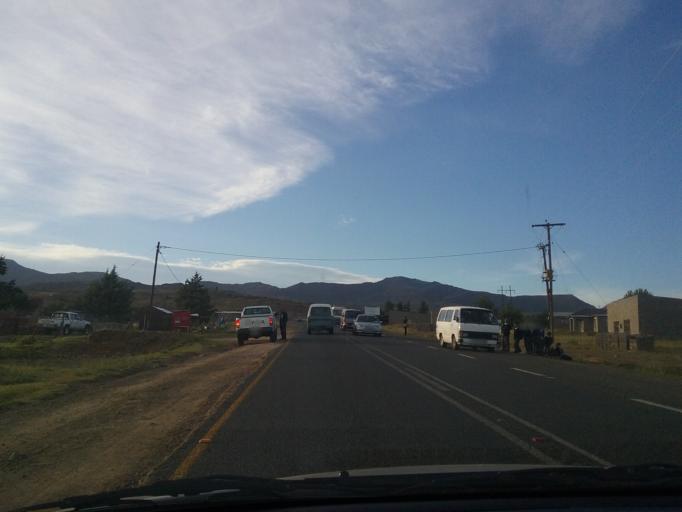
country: LS
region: Mohale's Hoek District
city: Mohale's Hoek
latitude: -30.1257
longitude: 27.4642
